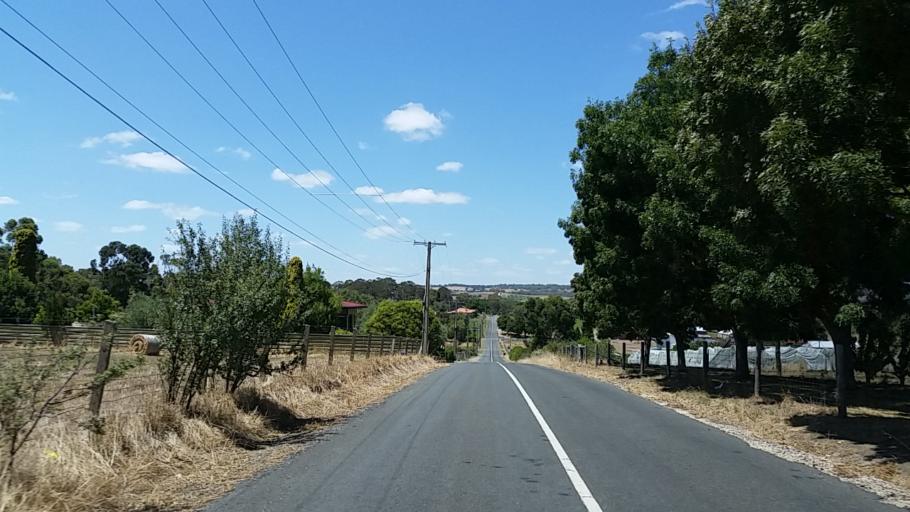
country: AU
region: South Australia
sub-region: Adelaide Hills
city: Lobethal
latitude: -34.9056
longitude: 138.8948
